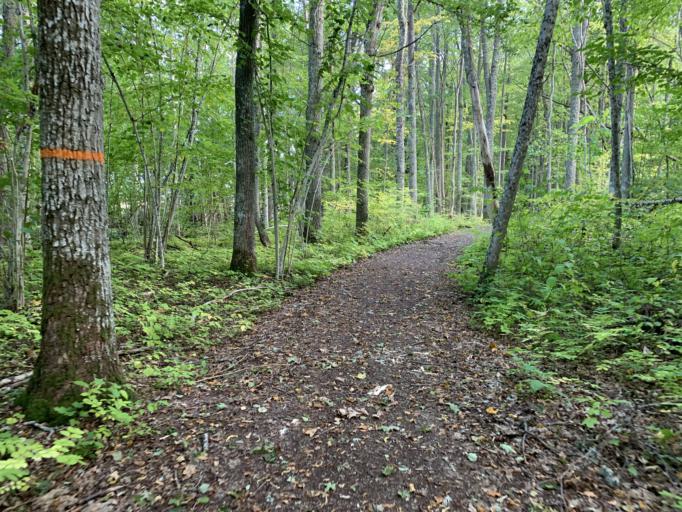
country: SE
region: Vaestmanland
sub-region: Hallstahammars Kommun
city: Kolback
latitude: 59.4794
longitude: 16.2122
